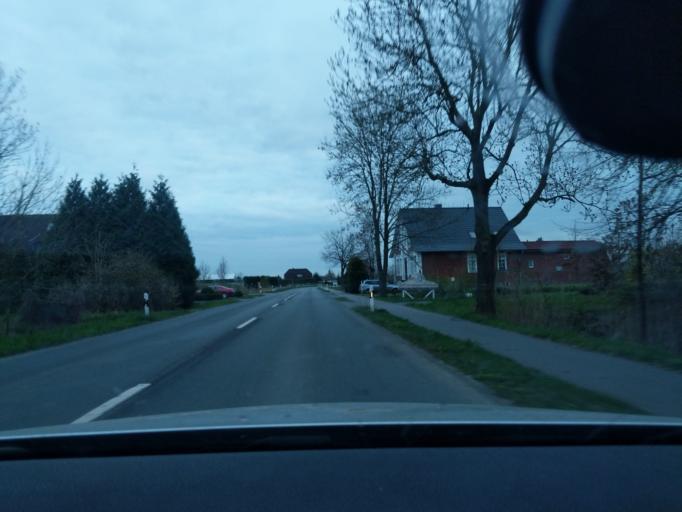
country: DE
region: Lower Saxony
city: Jork
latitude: 53.5209
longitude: 9.7360
